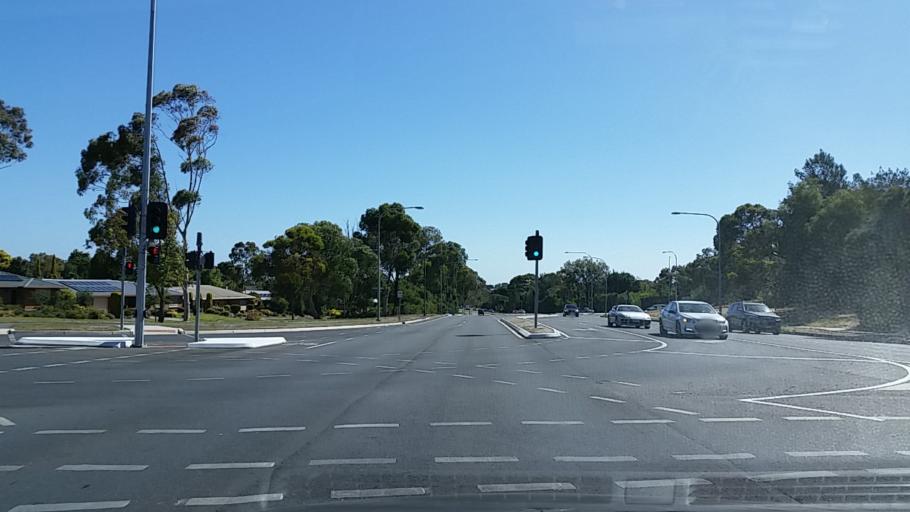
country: AU
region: South Australia
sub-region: Tea Tree Gully
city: Hope Valley
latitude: -34.8061
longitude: 138.7006
